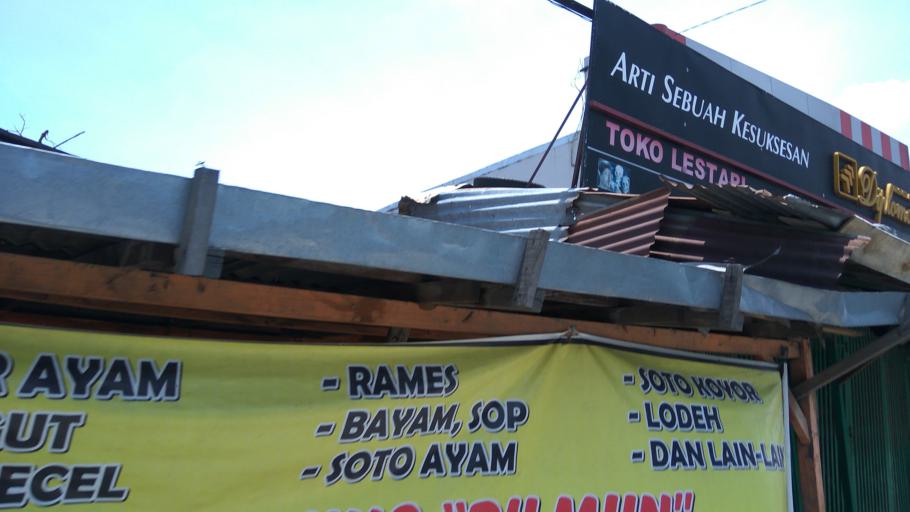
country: ID
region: Central Java
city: Mranggen
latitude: -7.0242
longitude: 110.5095
